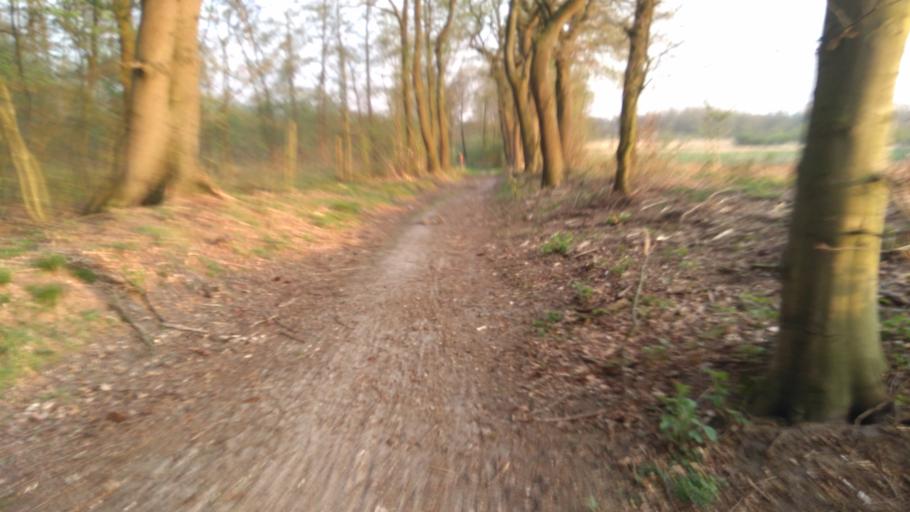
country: DE
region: Lower Saxony
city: Bliedersdorf
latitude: 53.4941
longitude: 9.5540
